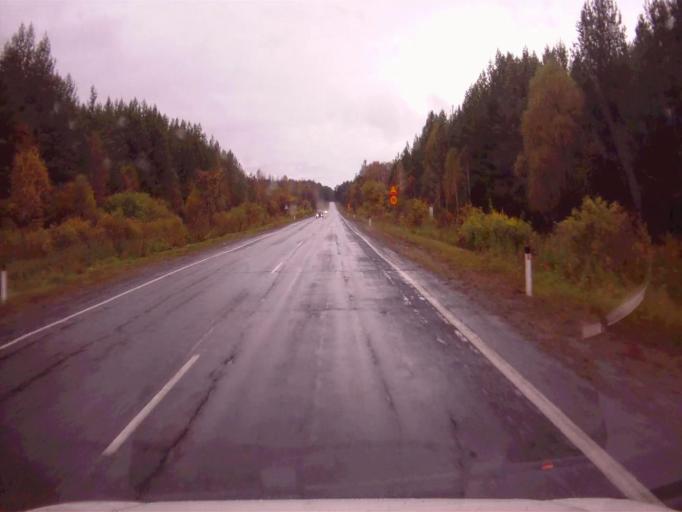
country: RU
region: Chelyabinsk
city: Verkhniy Ufaley
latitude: 56.0156
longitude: 60.3101
